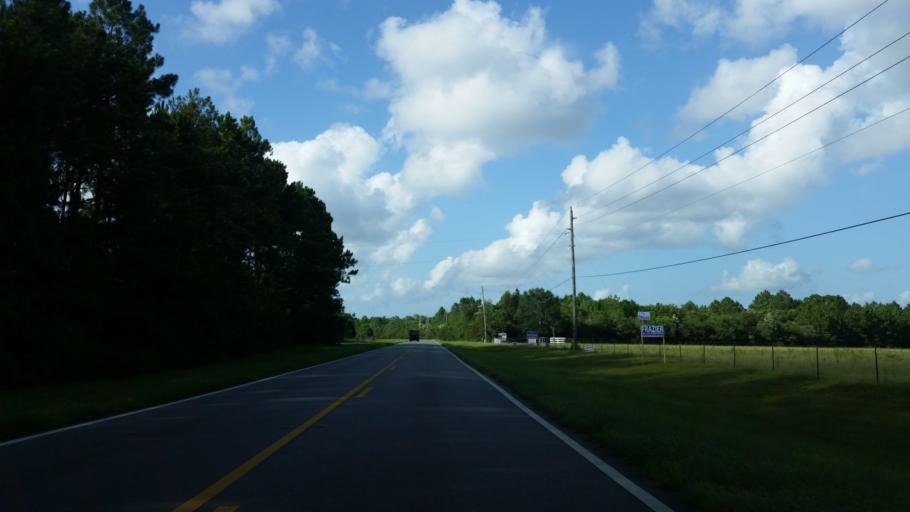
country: US
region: Florida
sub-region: Santa Rosa County
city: Bagdad
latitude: 30.5460
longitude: -87.0465
